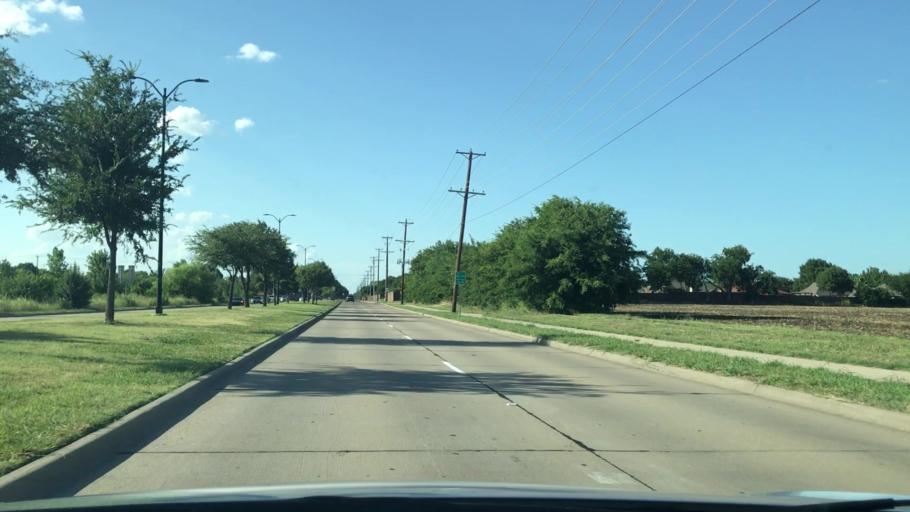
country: US
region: Texas
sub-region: Collin County
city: Frisco
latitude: 33.1063
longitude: -96.7882
